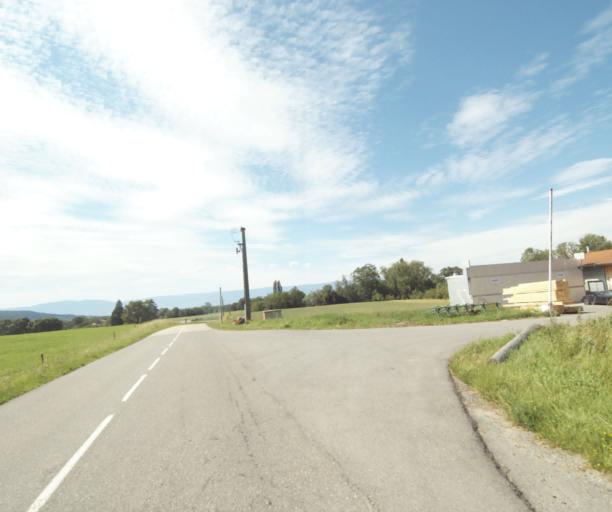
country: FR
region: Rhone-Alpes
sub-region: Departement de la Haute-Savoie
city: Perrignier
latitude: 46.2933
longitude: 6.4330
